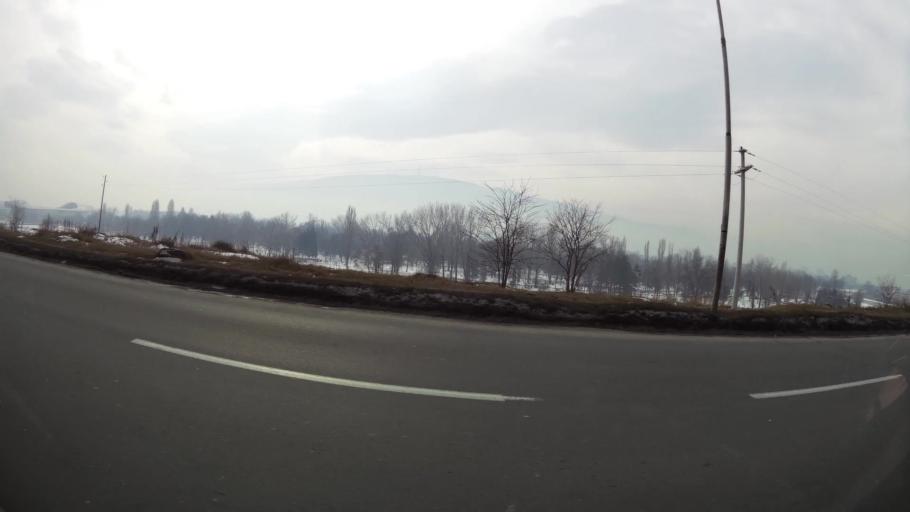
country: MK
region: Karpos
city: Skopje
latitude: 42.0133
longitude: 21.4197
